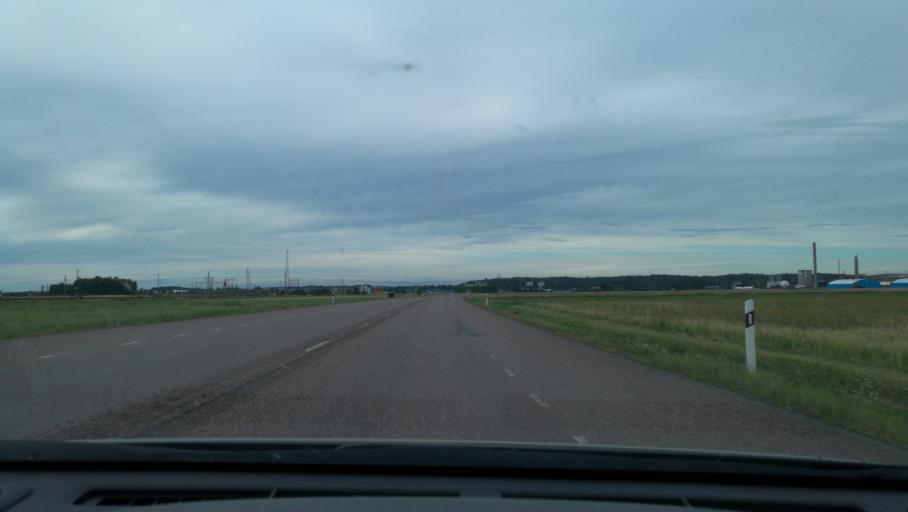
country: SE
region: Vaestmanland
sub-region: Kopings Kommun
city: Koping
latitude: 59.4889
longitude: 15.9870
